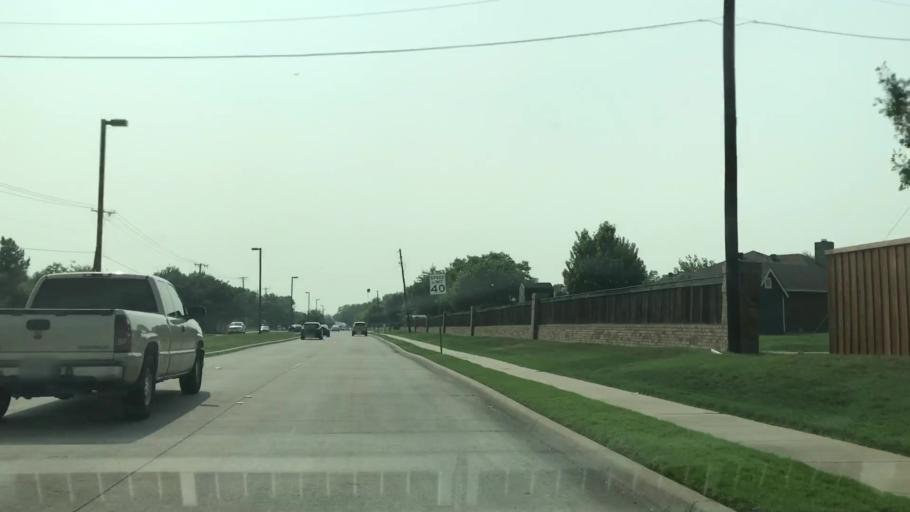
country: US
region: Texas
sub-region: Dallas County
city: Rowlett
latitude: 32.8941
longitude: -96.5765
